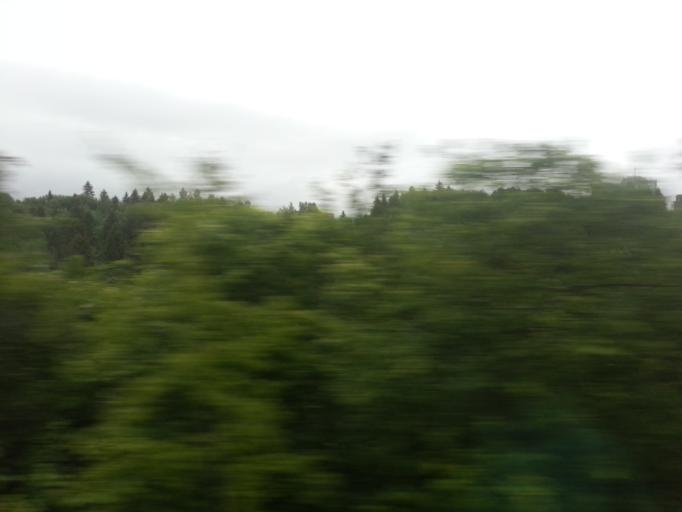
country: NO
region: Sor-Trondelag
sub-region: Trondheim
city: Trondheim
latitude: 63.3680
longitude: 10.3646
